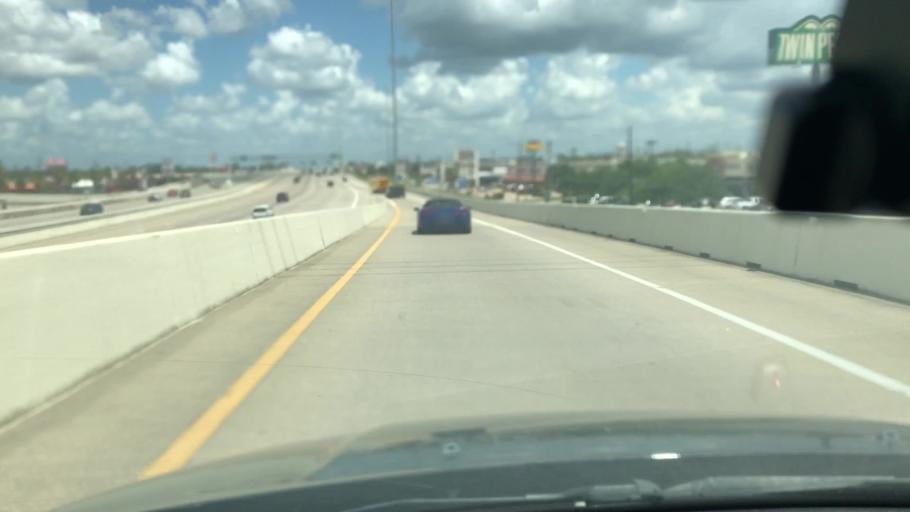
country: US
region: Texas
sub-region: Harris County
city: Webster
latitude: 29.5245
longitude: -95.1265
